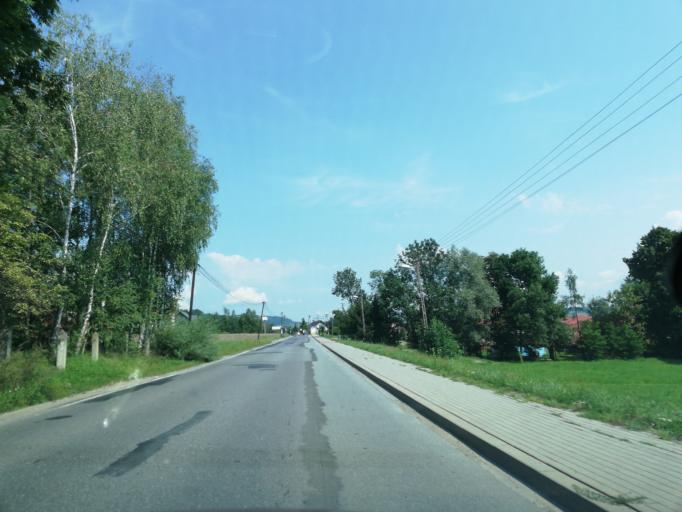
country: PL
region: Lesser Poland Voivodeship
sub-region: Powiat nowosadecki
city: Chelmiec
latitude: 49.6429
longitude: 20.6663
